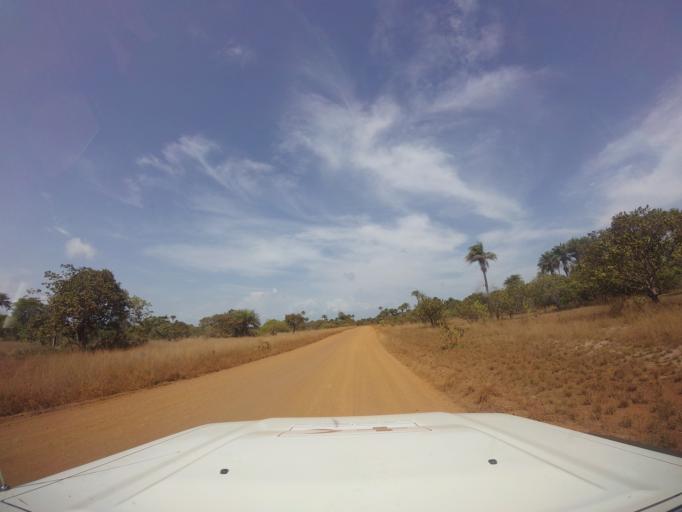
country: LR
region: Grand Cape Mount
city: Robertsport
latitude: 6.7060
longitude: -11.2998
